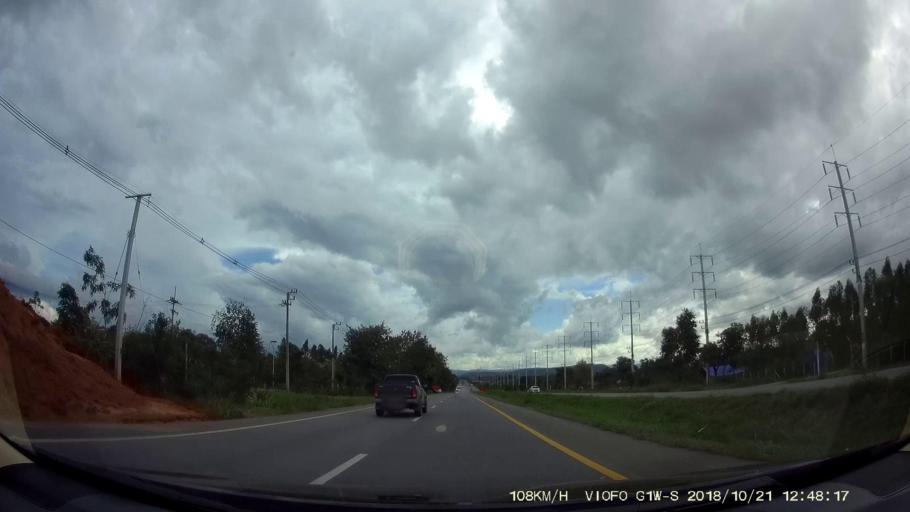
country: TH
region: Nakhon Ratchasima
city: Amphoe Sikhiu
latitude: 14.9148
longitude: 101.6840
